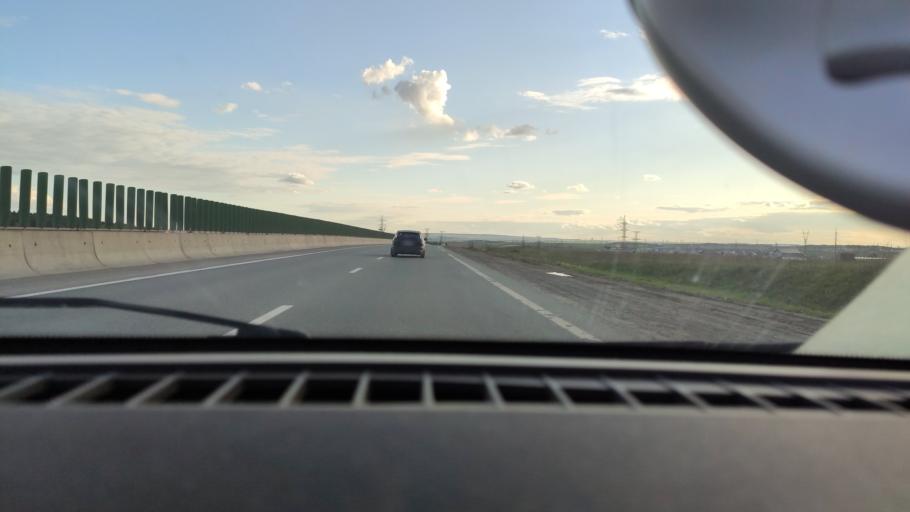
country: RU
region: Perm
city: Ferma
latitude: 57.9428
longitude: 56.3764
